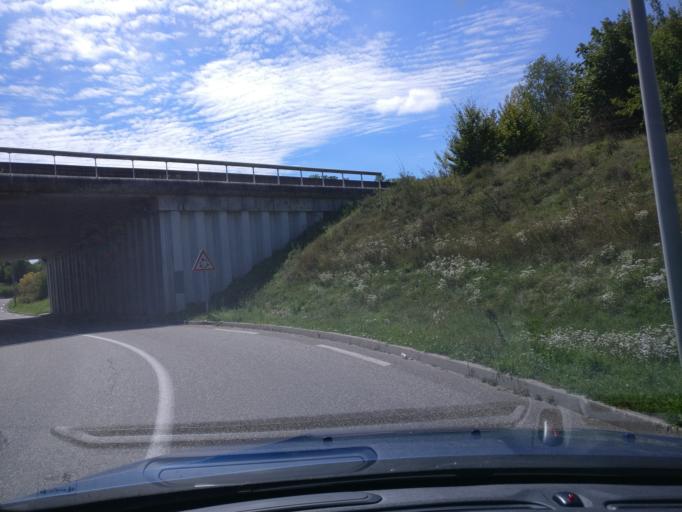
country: FR
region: Rhone-Alpes
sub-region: Departement de l'Ain
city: Saint-Genis-Pouilly
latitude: 46.2347
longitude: 6.0068
